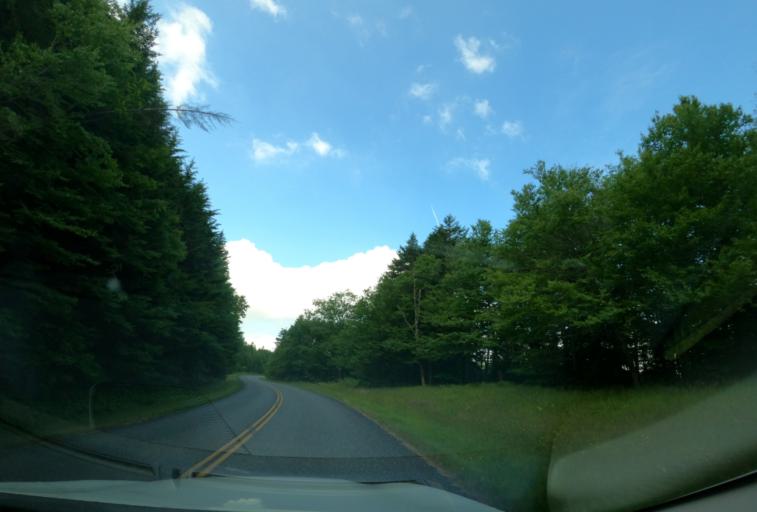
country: US
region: North Carolina
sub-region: Haywood County
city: Hazelwood
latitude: 35.3795
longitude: -83.0117
